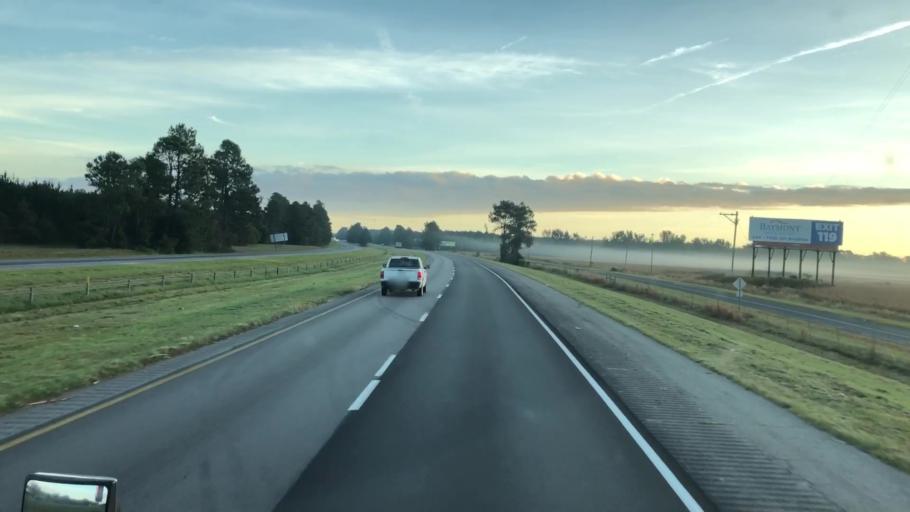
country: US
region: South Carolina
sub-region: Clarendon County
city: Manning
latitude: 33.5993
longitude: -80.3291
